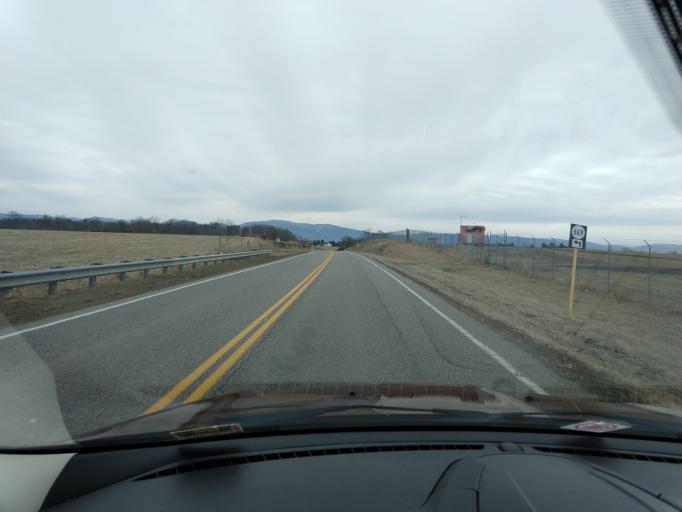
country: US
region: Virginia
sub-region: Augusta County
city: Weyers Cave
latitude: 38.2736
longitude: -78.8893
